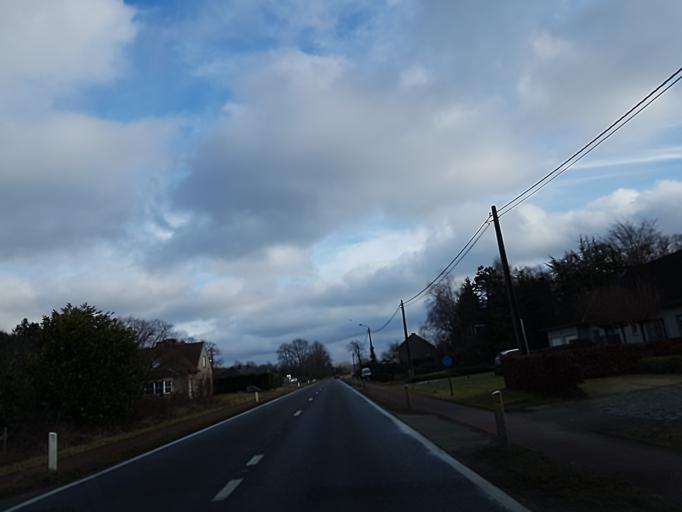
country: BE
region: Flanders
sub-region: Provincie Antwerpen
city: Herselt
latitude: 51.0716
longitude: 4.8804
